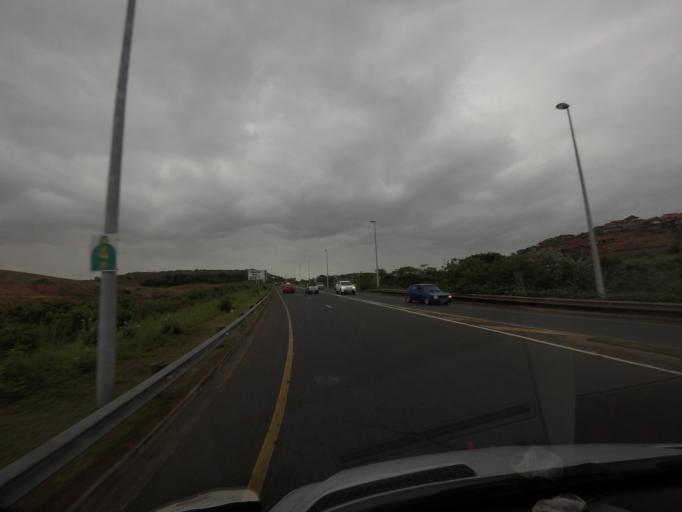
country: ZA
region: KwaZulu-Natal
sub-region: iLembe District Municipality
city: Ballitoville
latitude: -29.5637
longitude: 31.1836
